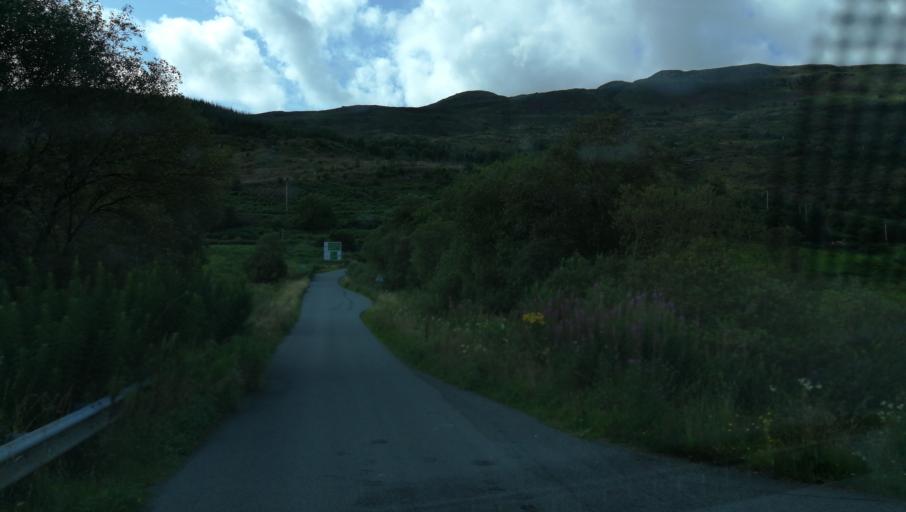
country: GB
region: Scotland
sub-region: Highland
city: Portree
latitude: 57.3871
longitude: -6.2012
